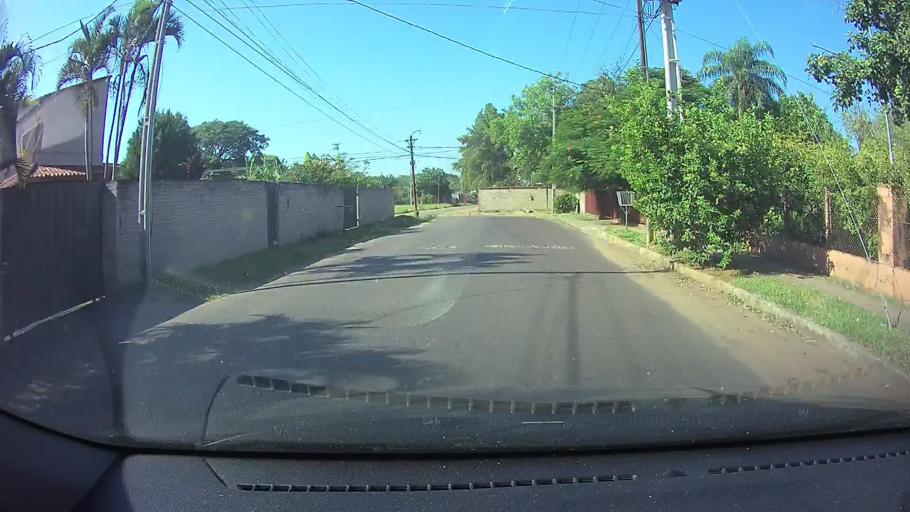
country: PY
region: Central
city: Fernando de la Mora
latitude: -25.2654
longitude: -57.5185
